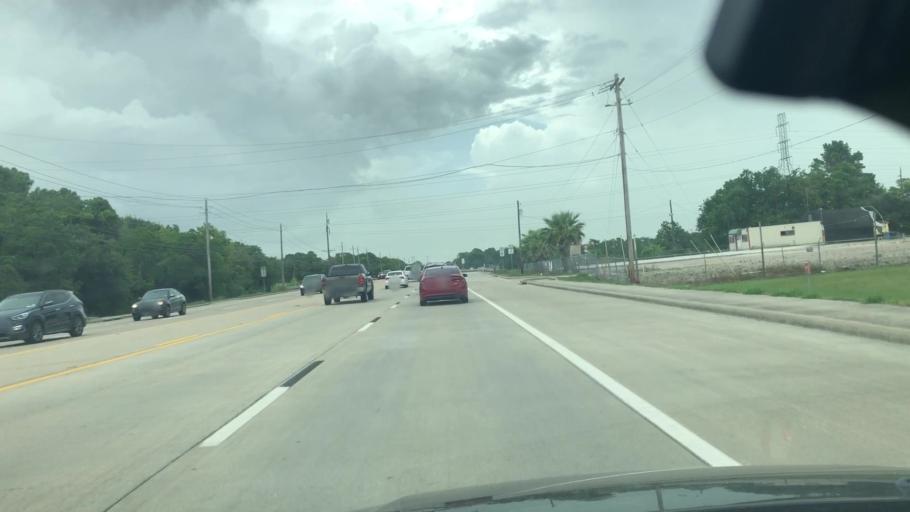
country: US
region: Texas
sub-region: Galveston County
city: Dickinson
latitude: 29.4767
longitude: -95.0751
